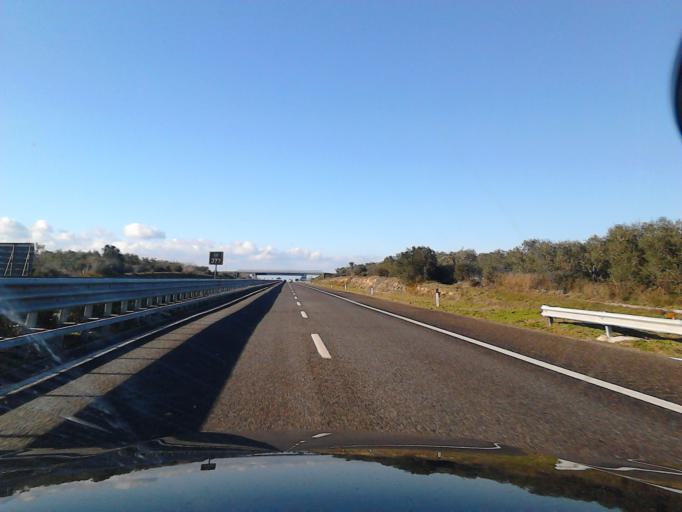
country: IT
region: Apulia
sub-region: Provincia di Foggia
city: Cerignola
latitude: 41.3262
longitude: 15.8886
